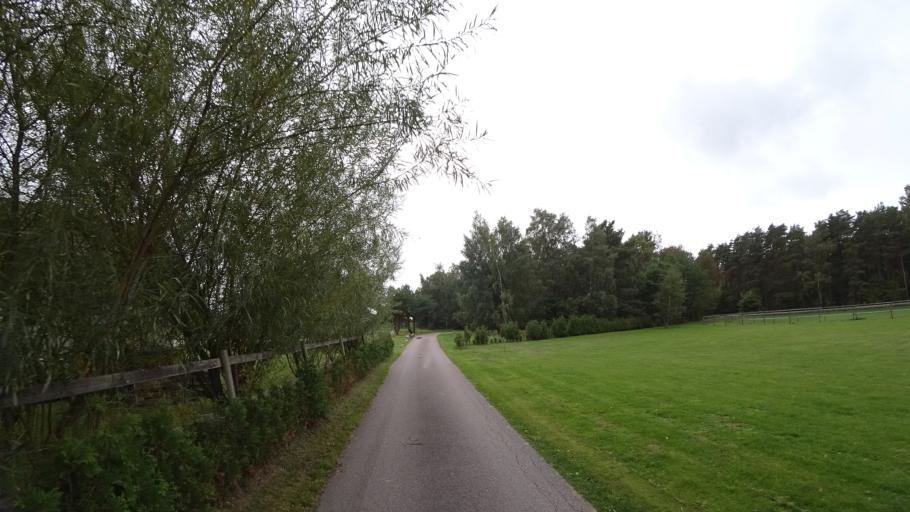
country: SE
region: Skane
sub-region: Kavlinge Kommun
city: Hofterup
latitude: 55.8012
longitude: 12.9947
